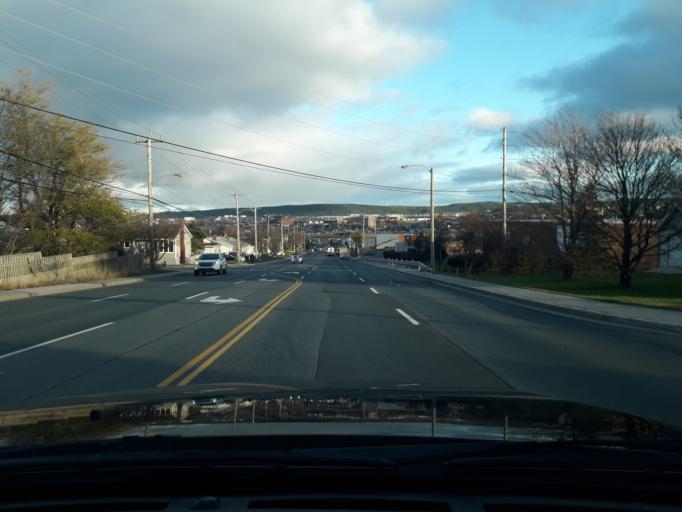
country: CA
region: Newfoundland and Labrador
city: St. John's
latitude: 47.5634
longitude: -52.7589
